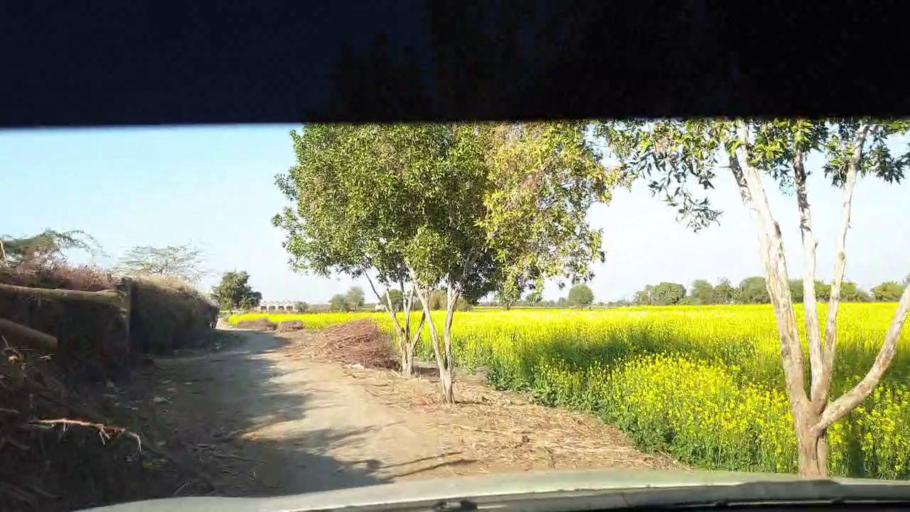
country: PK
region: Sindh
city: Berani
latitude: 25.7907
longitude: 68.9354
